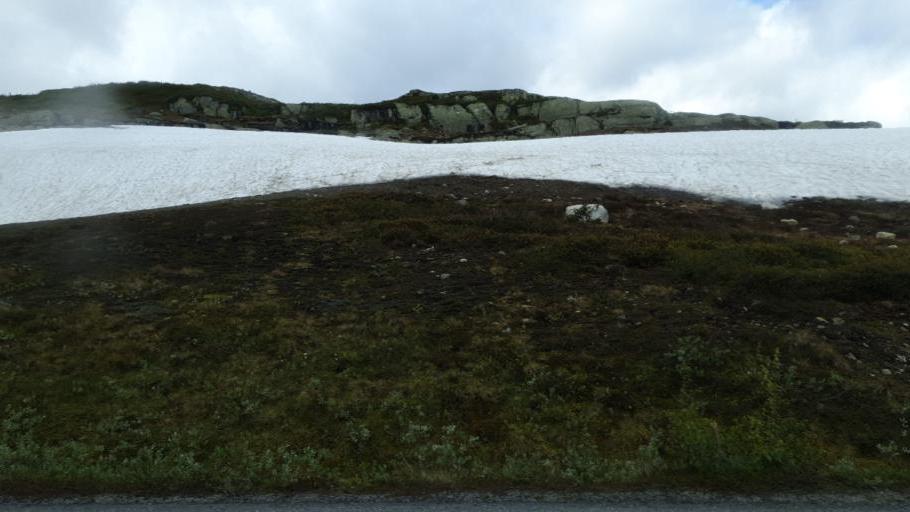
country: NO
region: Oppland
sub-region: Vestre Slidre
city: Slidre
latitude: 61.3147
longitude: 8.8080
